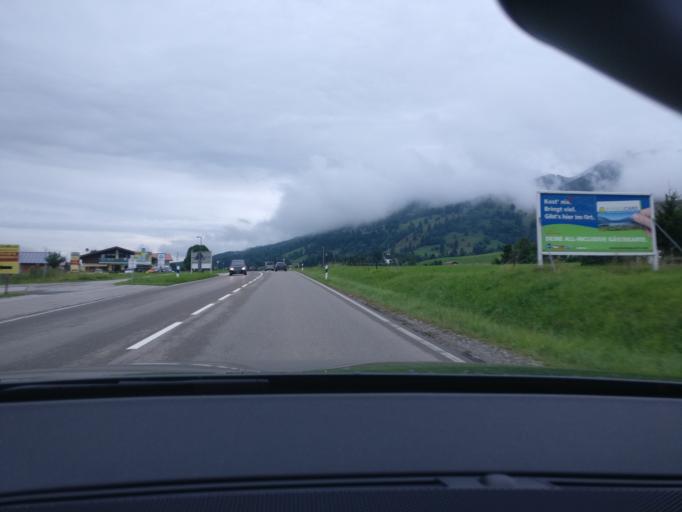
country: DE
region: Bavaria
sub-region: Upper Bavaria
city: Unterammergau
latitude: 47.6197
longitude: 11.0300
